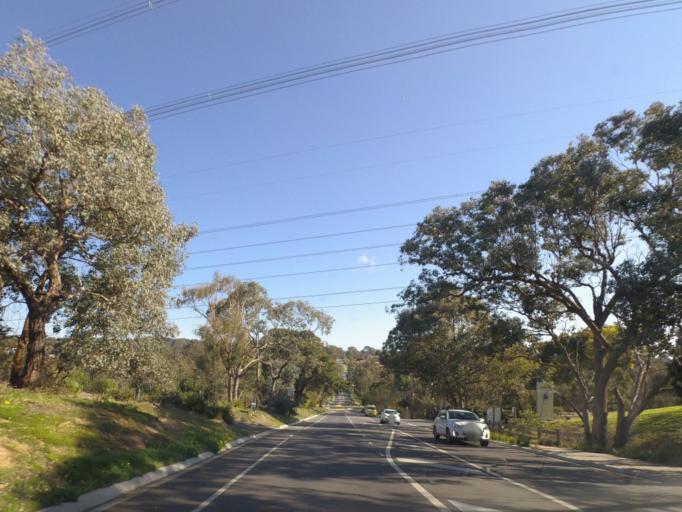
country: AU
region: Victoria
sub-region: Manningham
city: Park Orchards
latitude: -37.7751
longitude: 145.1929
